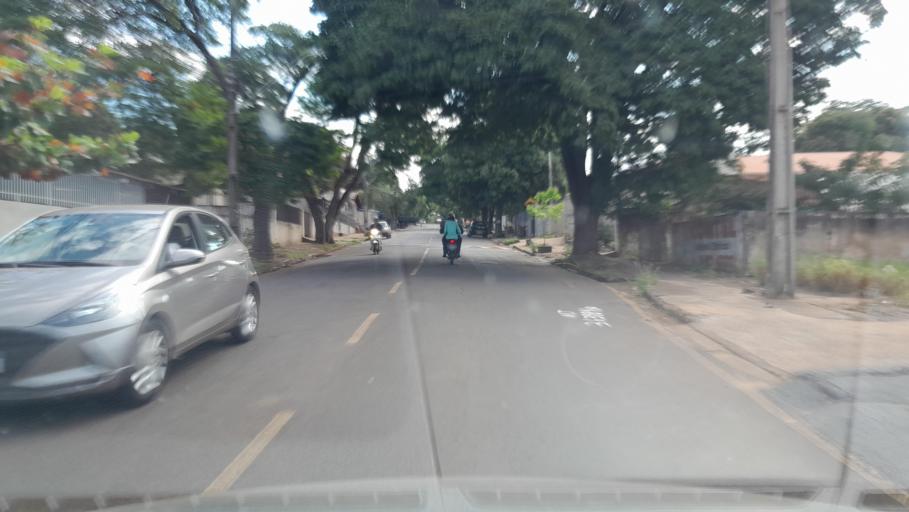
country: BR
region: Parana
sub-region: Umuarama
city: Umuarama
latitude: -23.7717
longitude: -53.3062
